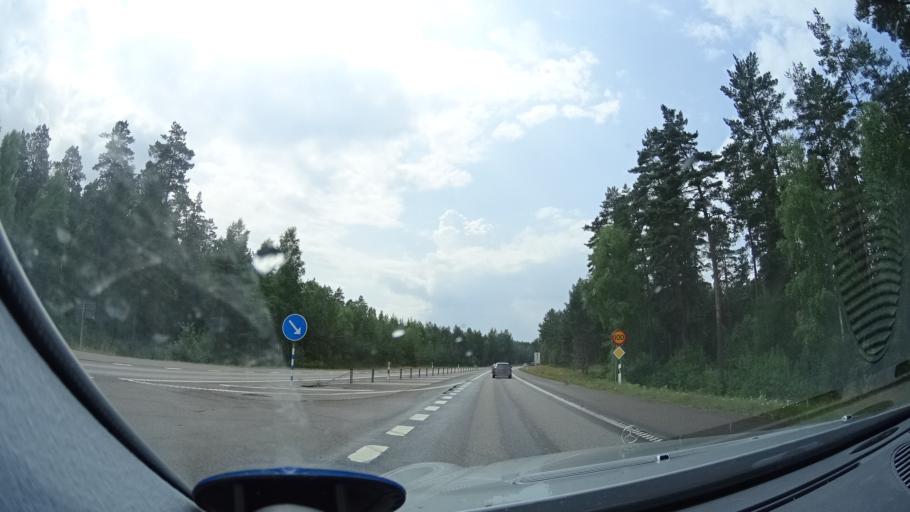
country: SE
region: Kalmar
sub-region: Nybro Kommun
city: Nybro
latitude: 56.7295
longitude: 15.9273
